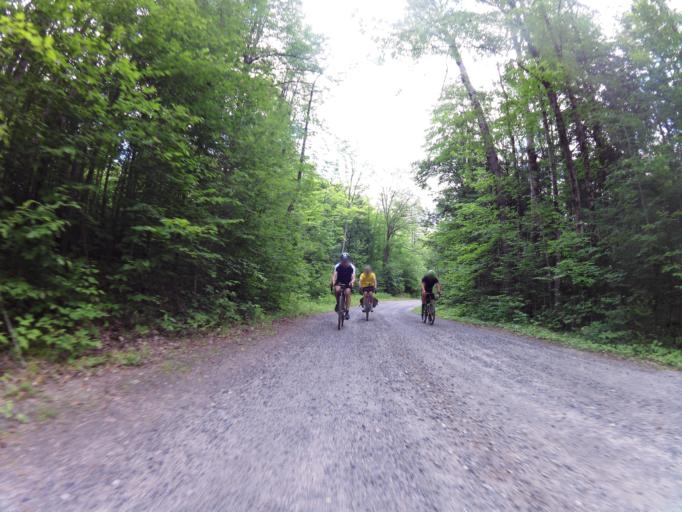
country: CA
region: Ontario
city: Perth
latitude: 45.0274
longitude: -76.5265
